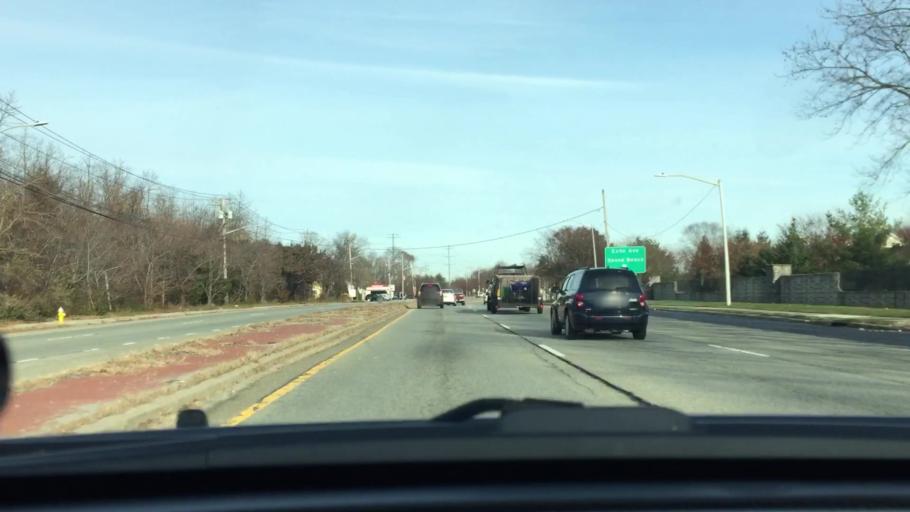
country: US
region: New York
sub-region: Suffolk County
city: Mount Sinai
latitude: 40.9389
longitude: -73.0082
